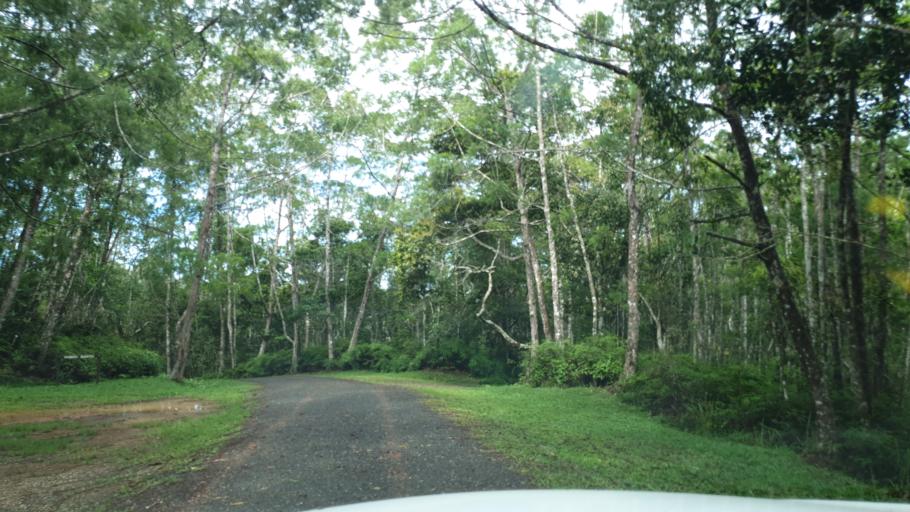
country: PG
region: National Capital
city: Port Moresby
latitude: -9.4345
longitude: 147.3658
